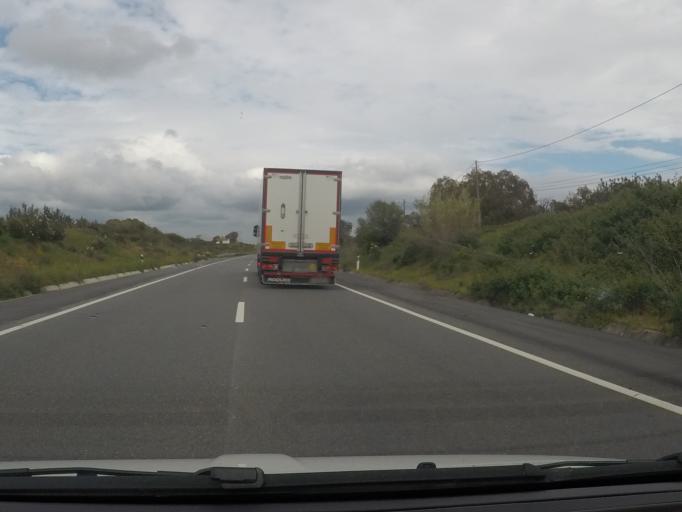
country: PT
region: Setubal
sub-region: Santiago do Cacem
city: Santiago do Cacem
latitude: 38.0708
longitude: -8.6699
